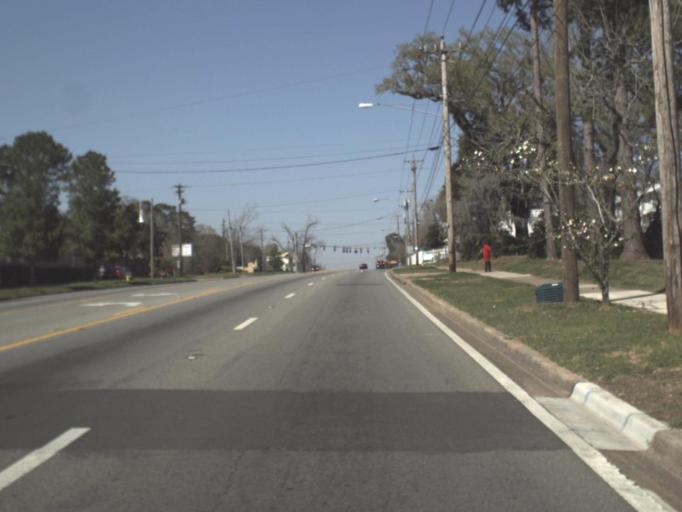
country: US
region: Florida
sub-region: Leon County
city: Tallahassee
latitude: 30.4212
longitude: -84.3023
